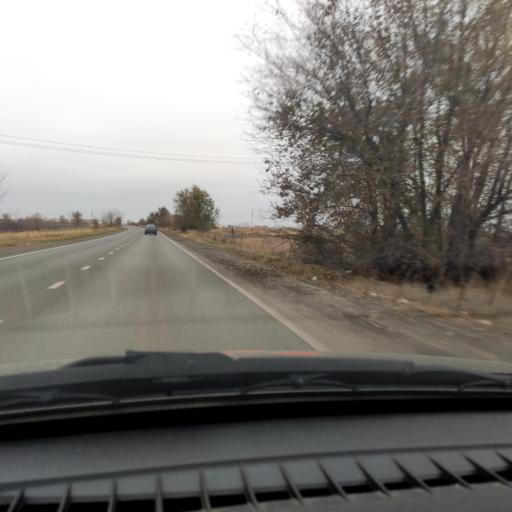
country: RU
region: Samara
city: Podstepki
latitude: 53.5174
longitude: 49.2120
